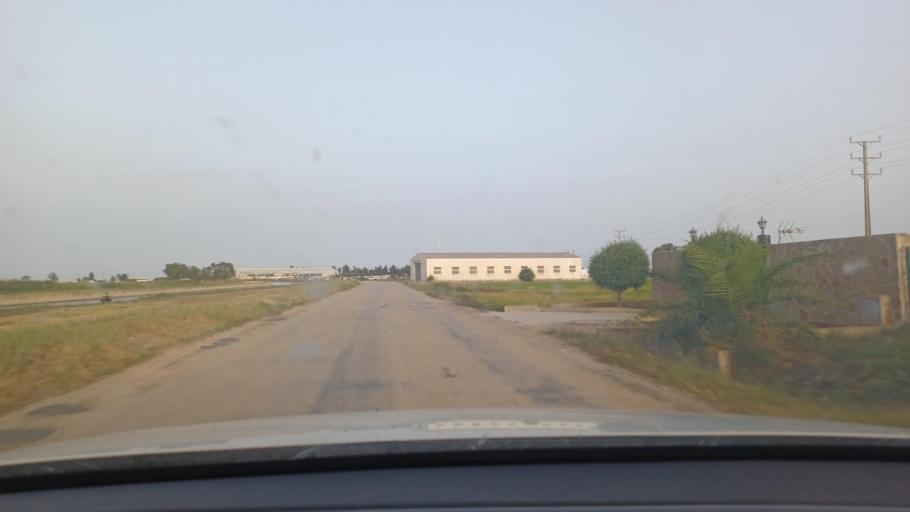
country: ES
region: Catalonia
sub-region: Provincia de Tarragona
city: Amposta
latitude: 40.7027
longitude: 0.5970
